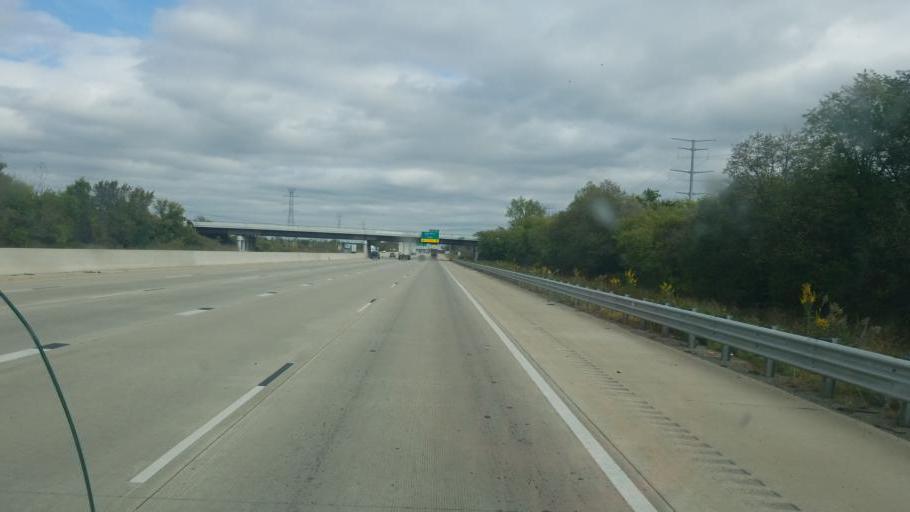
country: US
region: Michigan
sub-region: Monroe County
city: Woodland Beach
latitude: 41.9770
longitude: -83.3394
